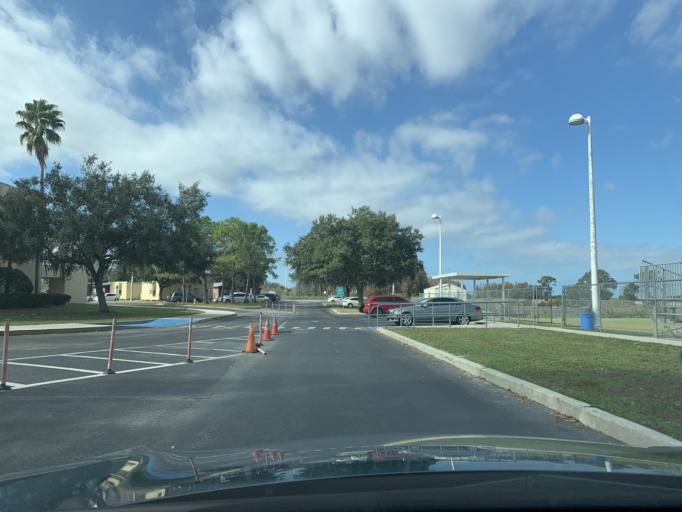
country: US
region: Florida
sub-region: Pasco County
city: Trinity
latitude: 28.1964
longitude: -82.6707
